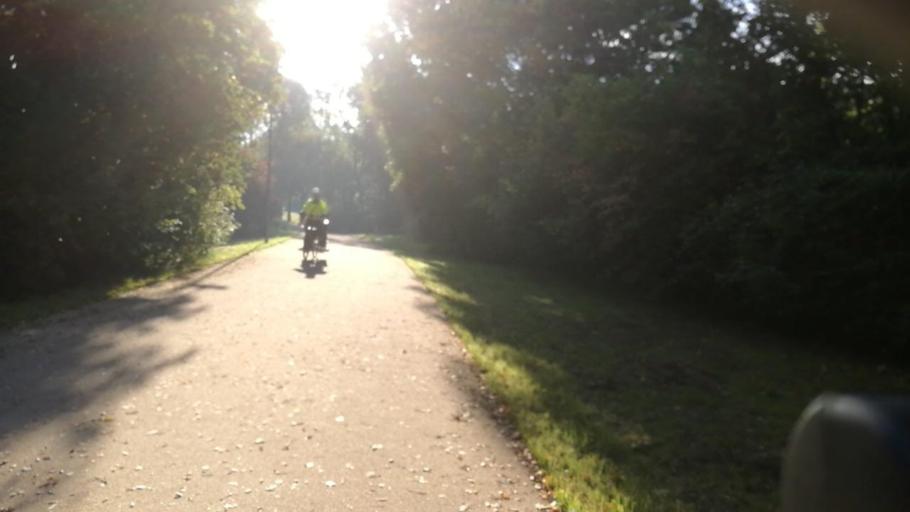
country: DE
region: North Rhine-Westphalia
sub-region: Regierungsbezirk Detmold
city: Bielefeld
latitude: 52.0063
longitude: 8.5733
